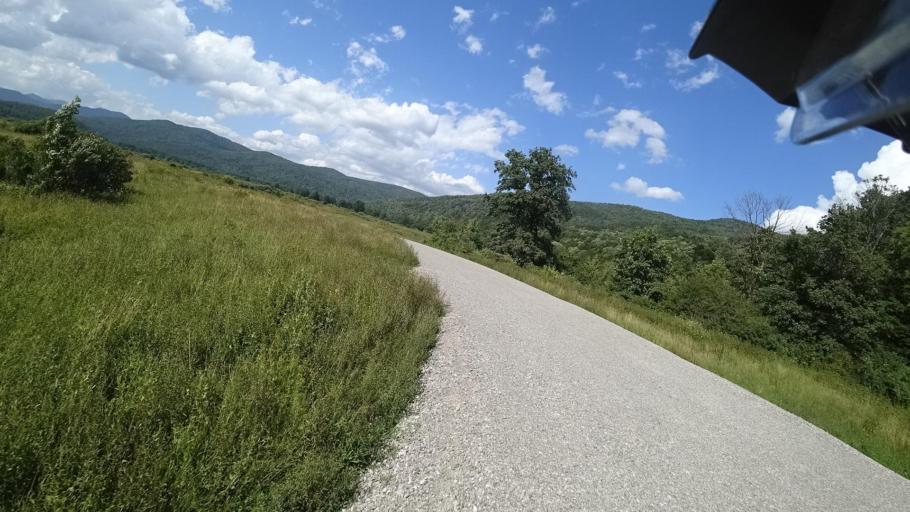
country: HR
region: Licko-Senjska
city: Brinje
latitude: 45.1438
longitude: 15.1107
